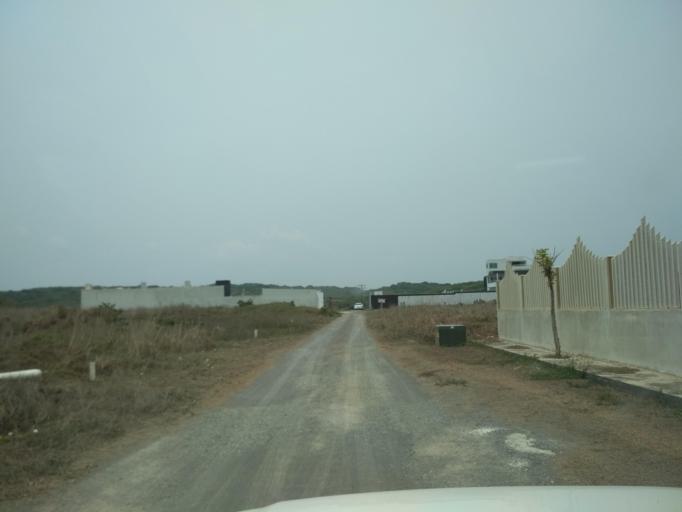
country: MX
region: Veracruz
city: Anton Lizardo
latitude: 19.0567
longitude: -96.0422
